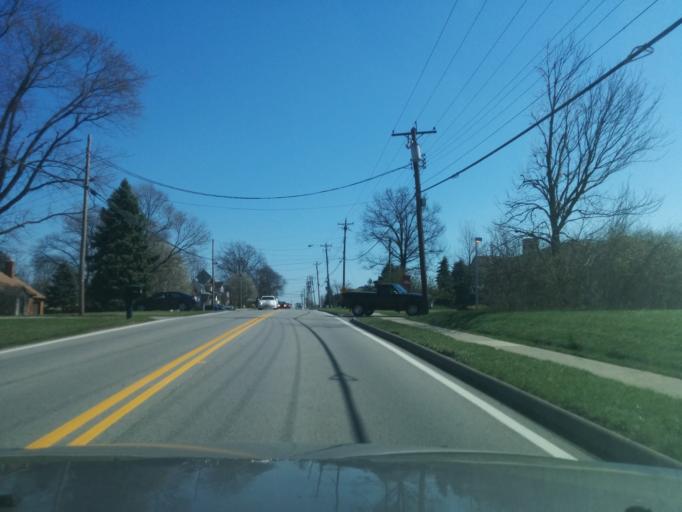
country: US
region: Ohio
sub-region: Hamilton County
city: Monfort Heights
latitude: 39.1894
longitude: -84.6099
